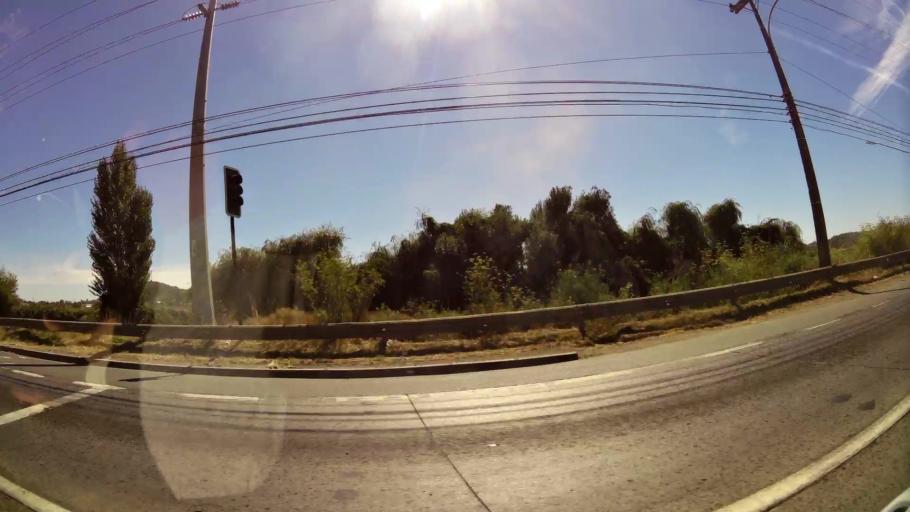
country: CL
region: Biobio
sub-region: Provincia de Concepcion
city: Concepcion
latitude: -36.7918
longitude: -73.0253
